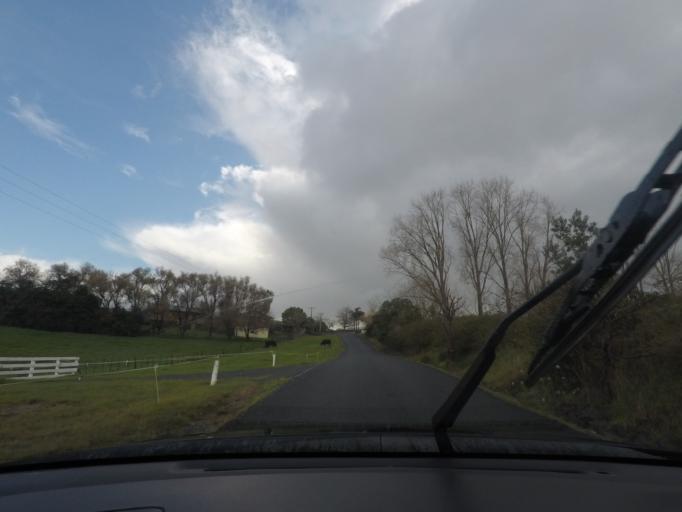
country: NZ
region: Auckland
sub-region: Auckland
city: Warkworth
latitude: -36.4304
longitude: 174.7317
